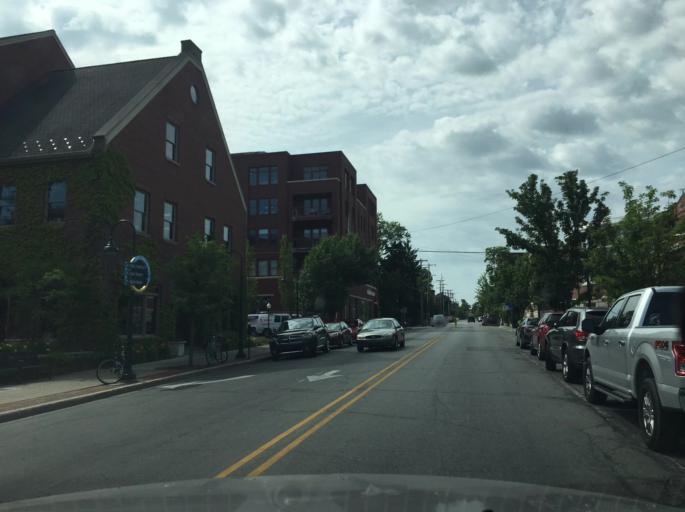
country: US
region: Michigan
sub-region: Grand Traverse County
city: Traverse City
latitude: 44.7628
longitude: -85.6211
